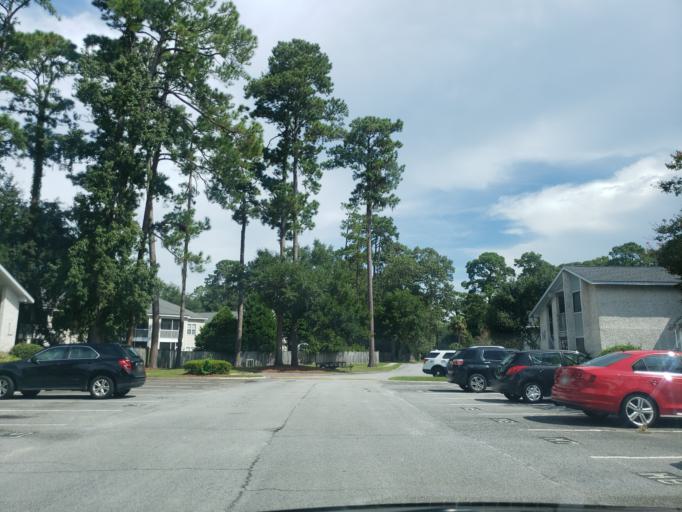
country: US
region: Georgia
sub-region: Chatham County
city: Wilmington Island
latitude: 32.0267
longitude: -80.9644
